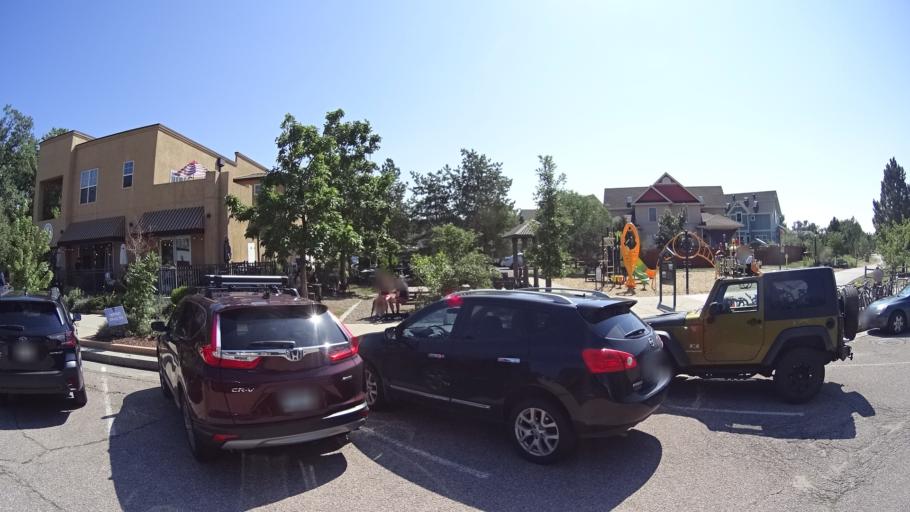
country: US
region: Colorado
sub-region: El Paso County
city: Colorado Springs
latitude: 38.8534
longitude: -104.8153
